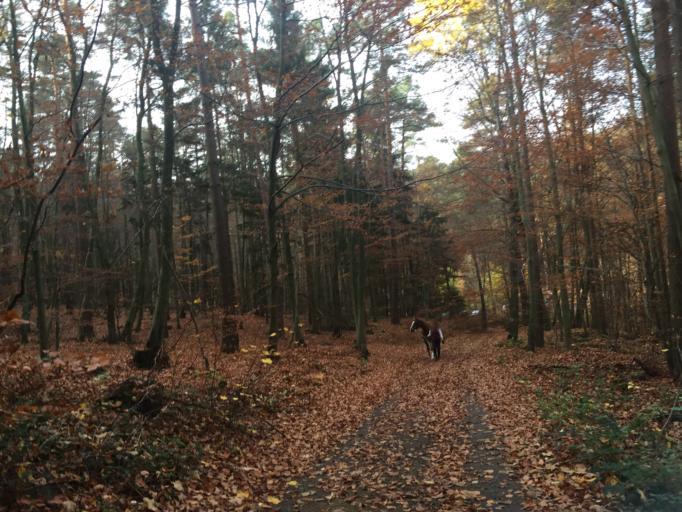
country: DE
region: Rheinland-Pfalz
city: Altleiningen
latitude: 49.4889
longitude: 8.0736
